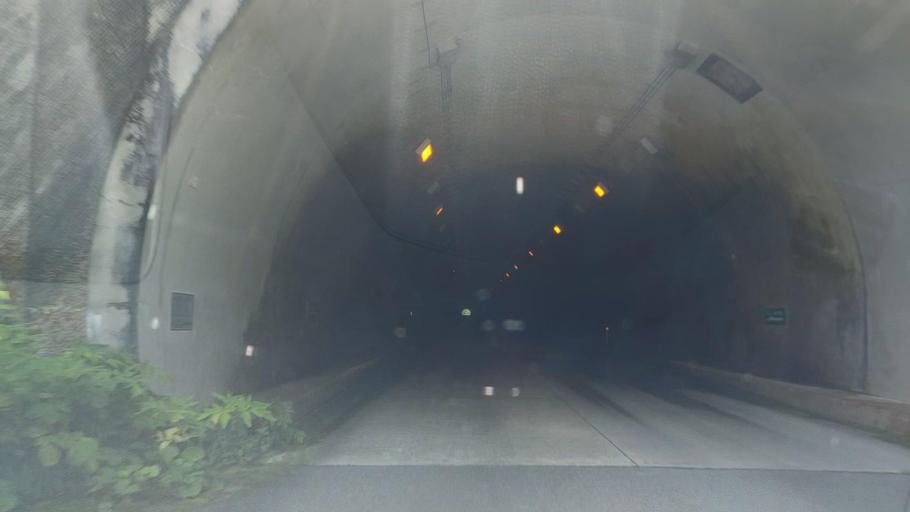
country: JP
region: Fukui
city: Ono
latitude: 35.8490
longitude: 136.4573
